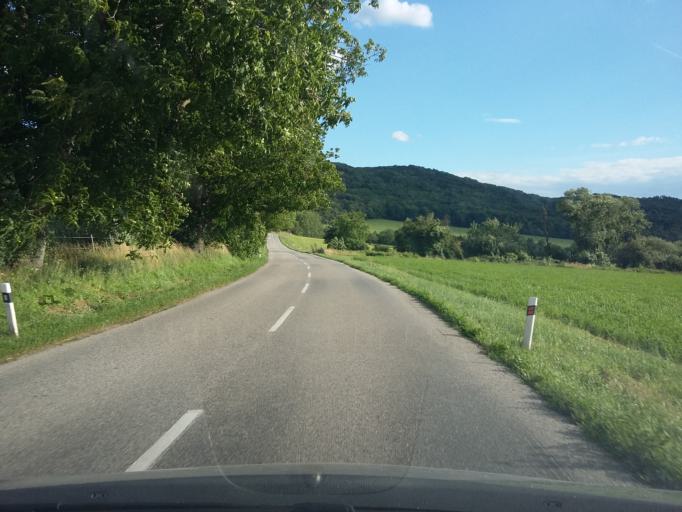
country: SK
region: Trnavsky
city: Smolenice
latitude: 48.5482
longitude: 17.3489
